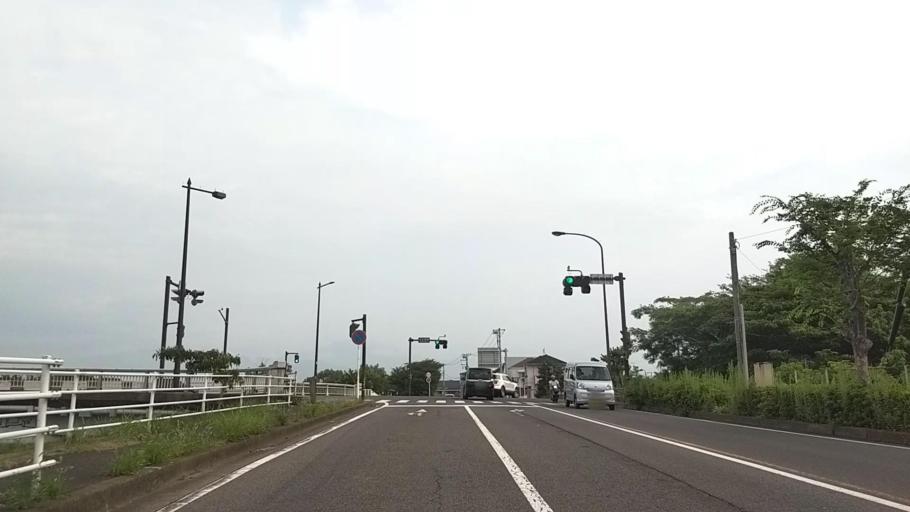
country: JP
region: Kanagawa
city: Hiratsuka
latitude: 35.3232
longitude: 139.3298
